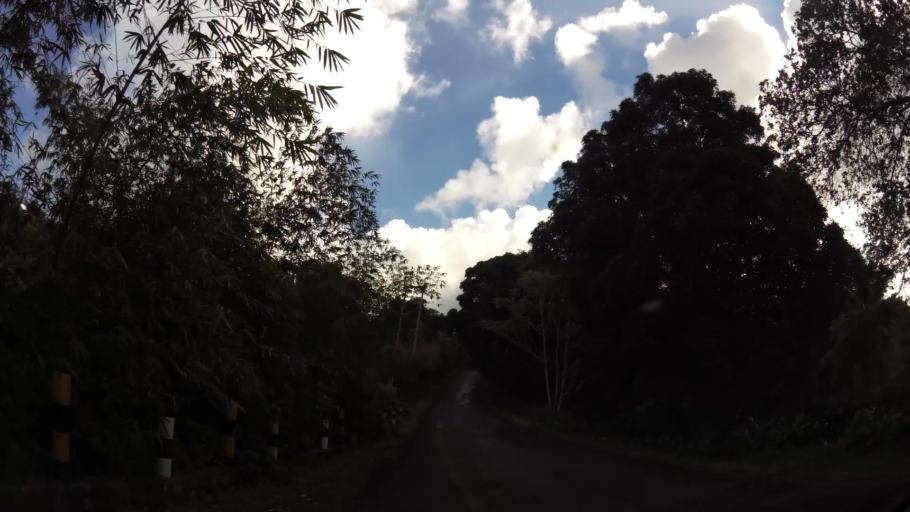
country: DM
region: Saint Andrew
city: Calibishie
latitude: 15.5964
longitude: -61.3949
